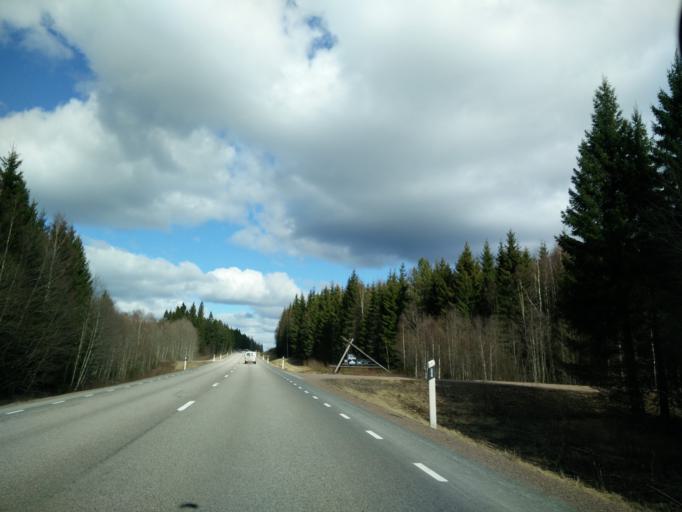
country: SE
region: Vaermland
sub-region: Hagfors Kommun
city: Hagfors
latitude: 59.9886
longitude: 13.5869
